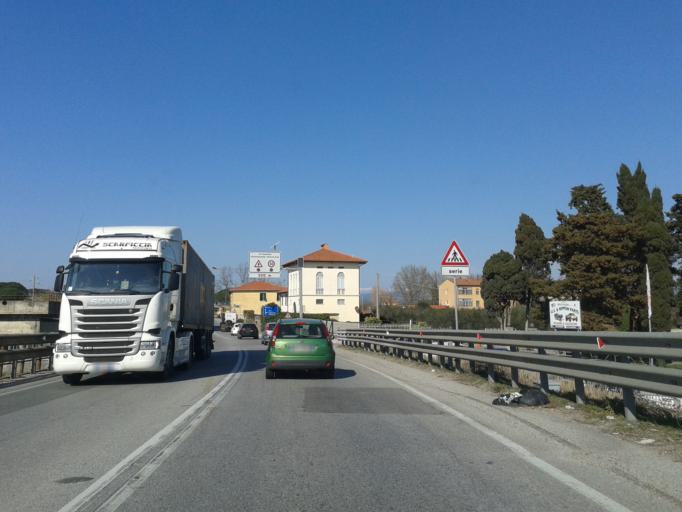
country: IT
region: Tuscany
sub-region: Provincia di Livorno
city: Guasticce
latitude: 43.6007
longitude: 10.3525
